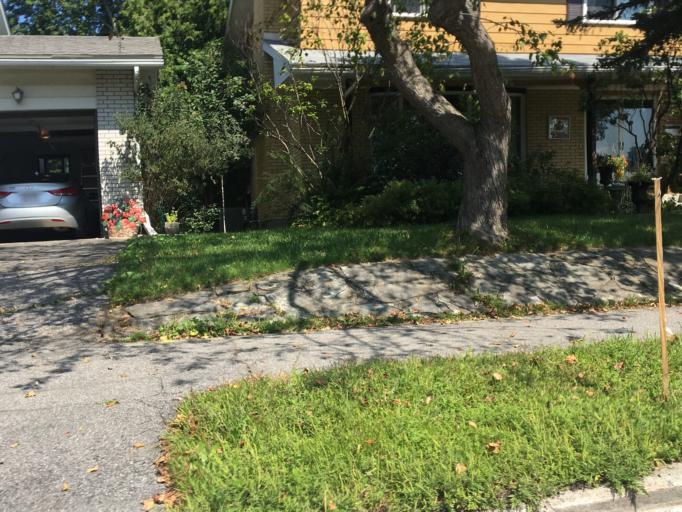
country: CA
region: Ontario
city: Ottawa
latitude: 45.3833
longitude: -75.6414
